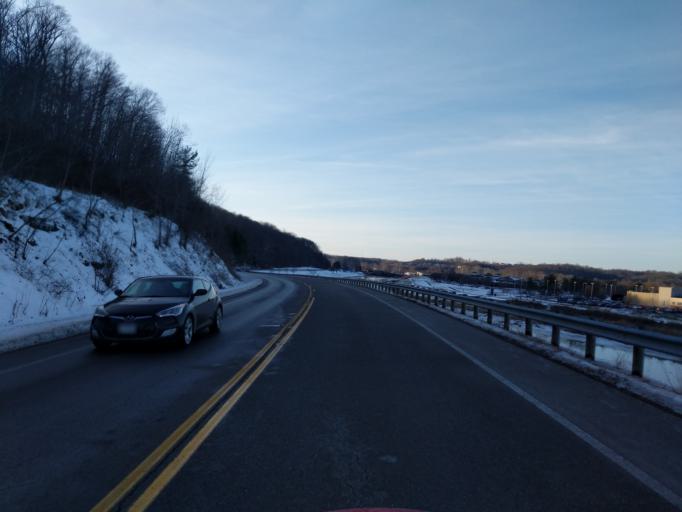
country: US
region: Ohio
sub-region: Athens County
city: Athens
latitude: 39.3247
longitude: -82.1136
